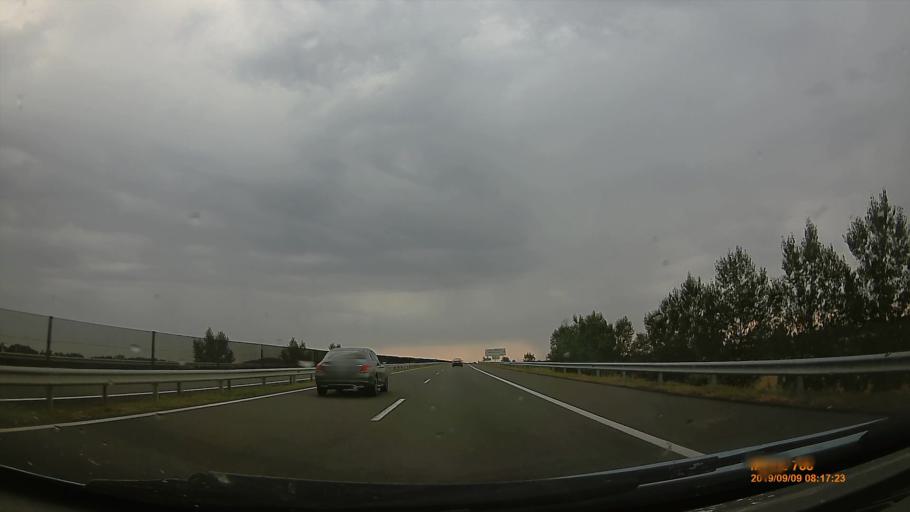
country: HU
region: Hajdu-Bihar
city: Hajdunanas
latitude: 47.8790
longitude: 21.3998
